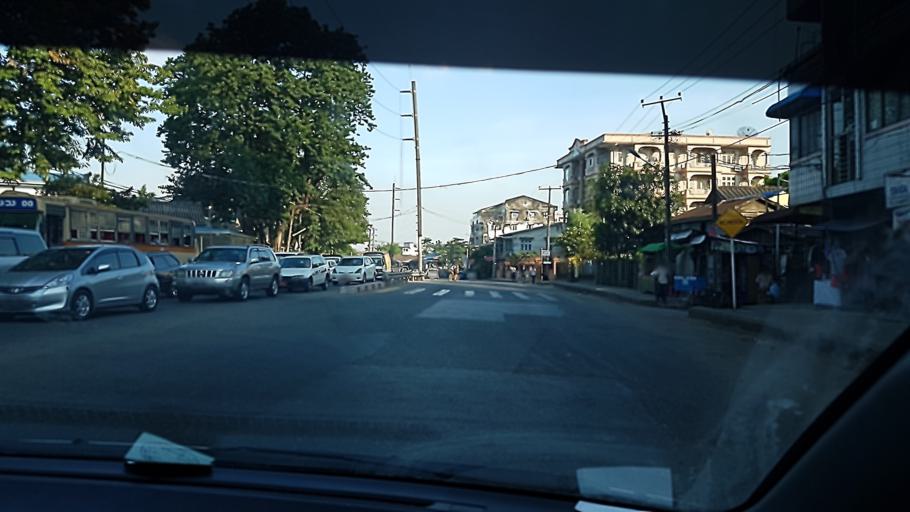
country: MM
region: Yangon
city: Yangon
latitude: 16.8202
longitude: 96.1773
